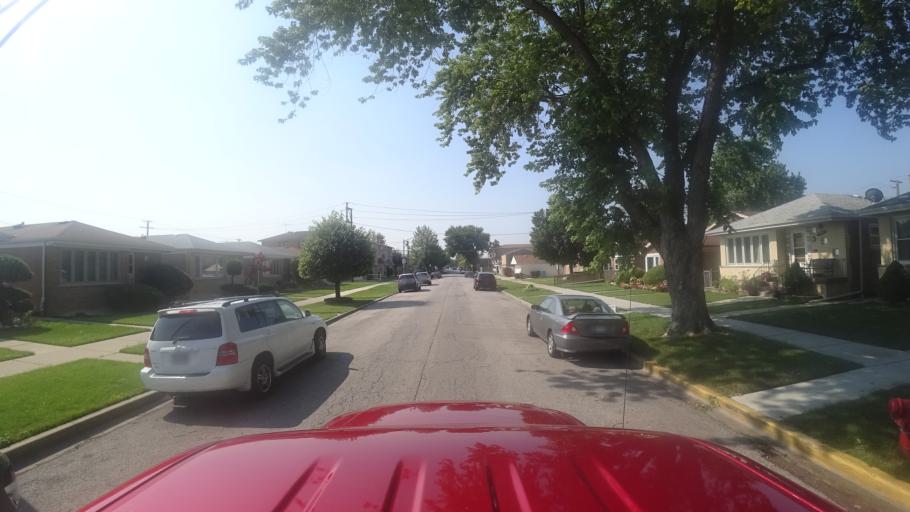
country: US
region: Illinois
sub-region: Cook County
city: Cicero
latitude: 41.8014
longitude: -87.7393
